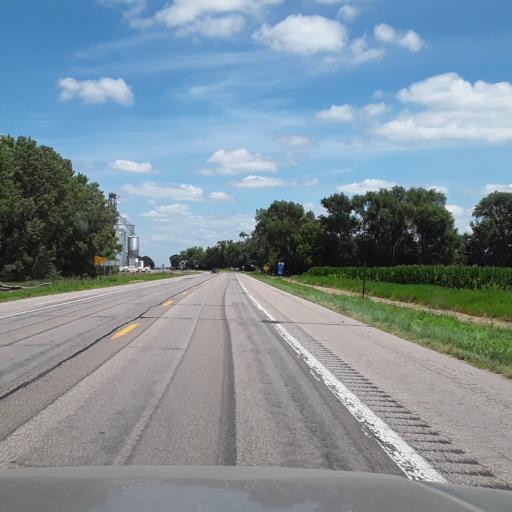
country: US
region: Nebraska
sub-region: Platte County
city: Columbus
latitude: 41.3855
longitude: -97.4999
